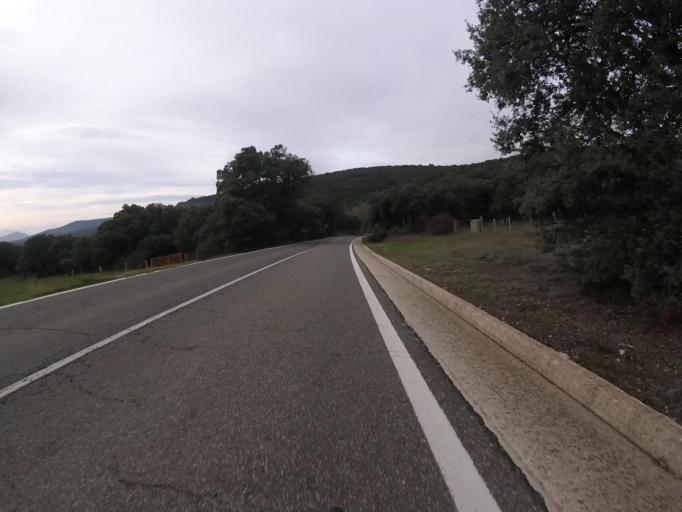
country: ES
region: Navarre
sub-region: Provincia de Navarra
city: Lezaun
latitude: 42.7541
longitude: -2.0141
